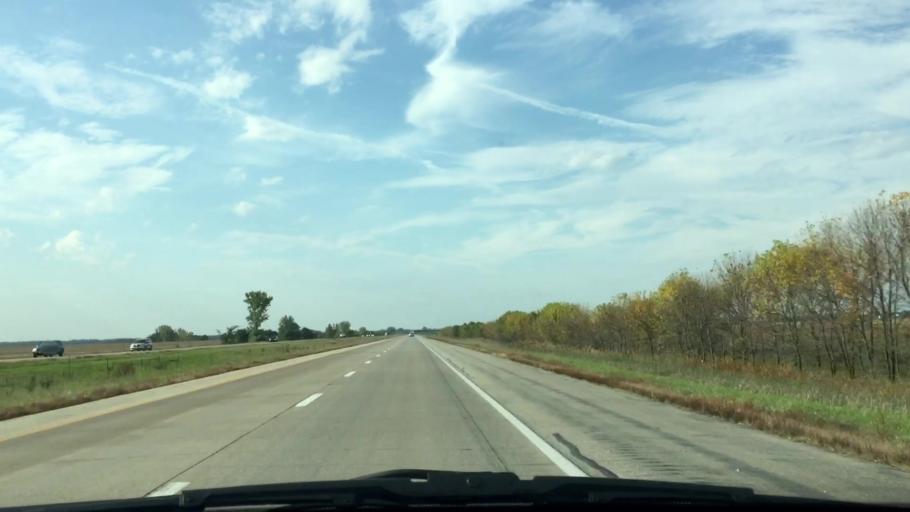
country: US
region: Illinois
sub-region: Whiteside County
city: Erie
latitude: 41.6593
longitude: -90.1471
